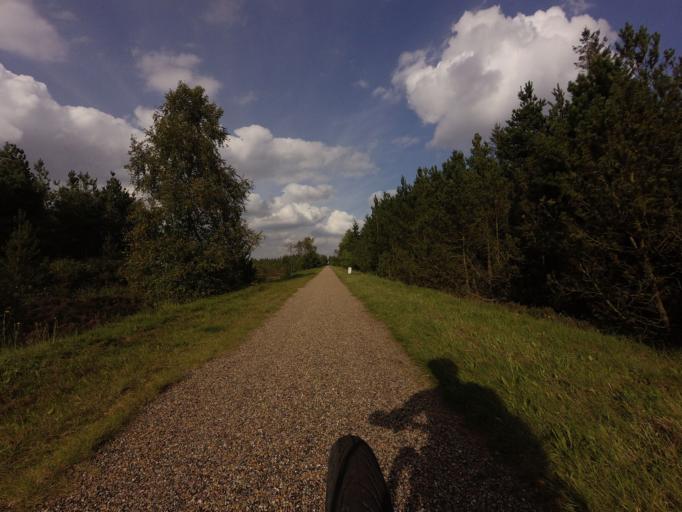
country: DK
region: Central Jutland
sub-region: Viborg Kommune
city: Karup
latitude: 56.2444
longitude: 9.0979
